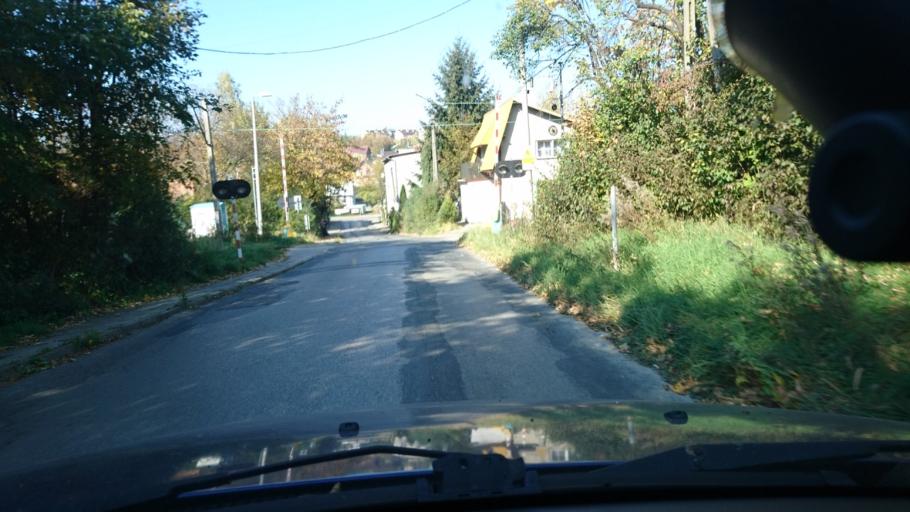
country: PL
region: Silesian Voivodeship
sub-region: Bielsko-Biala
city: Bielsko-Biala
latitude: 49.8294
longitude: 19.0327
